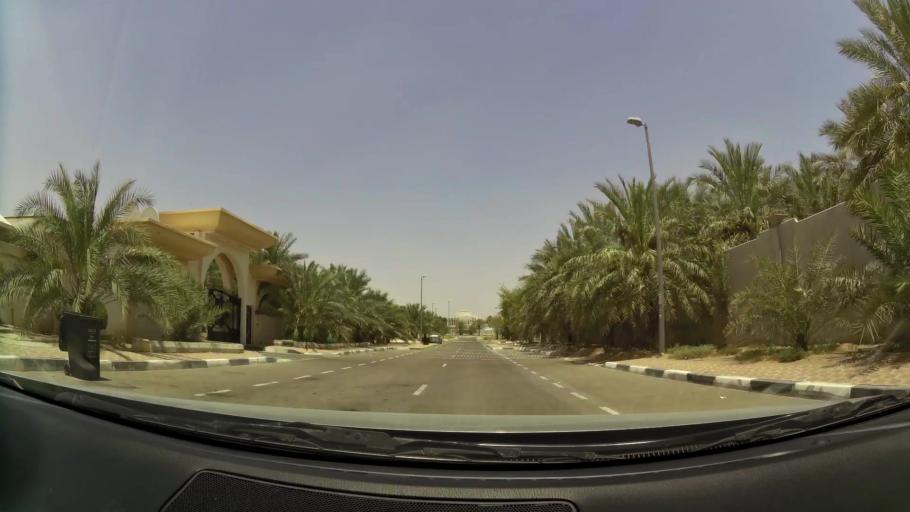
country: OM
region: Al Buraimi
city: Al Buraymi
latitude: 24.2668
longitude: 55.7187
